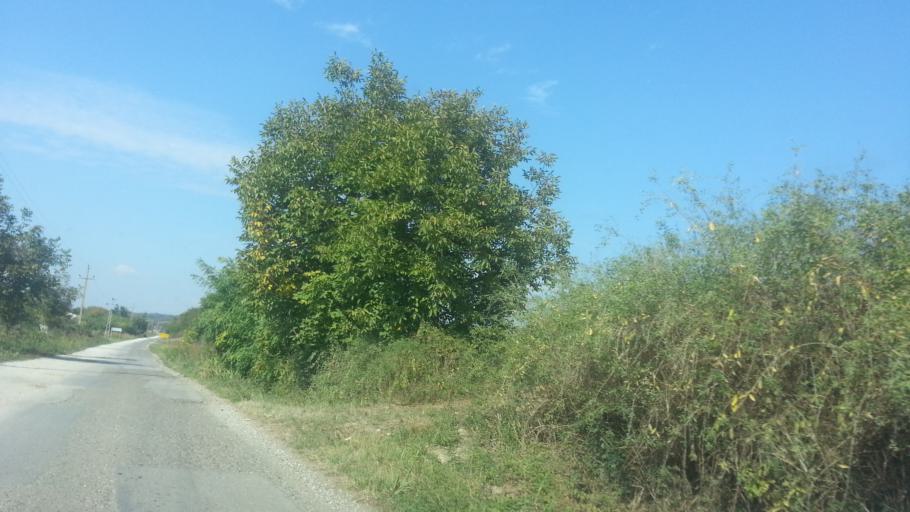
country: RS
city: Novi Slankamen
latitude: 45.1267
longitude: 20.2601
